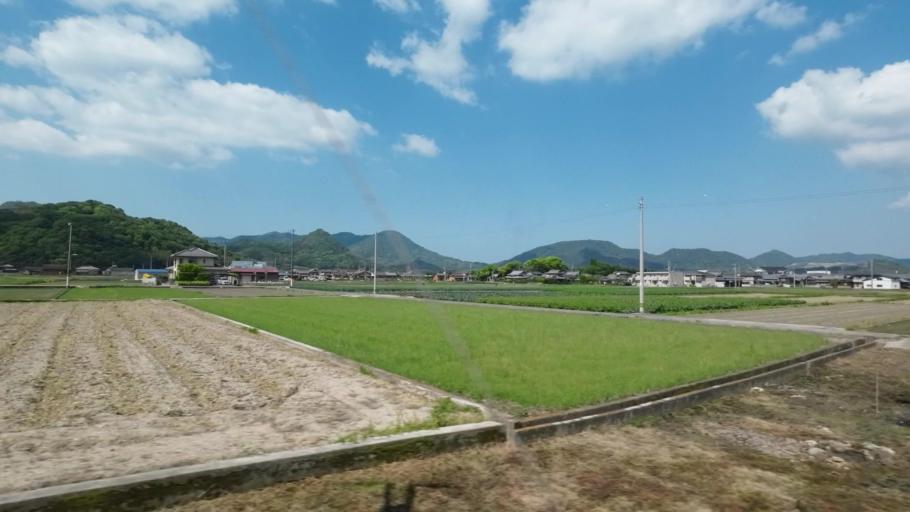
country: JP
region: Kagawa
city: Tadotsu
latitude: 34.2014
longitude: 133.7123
